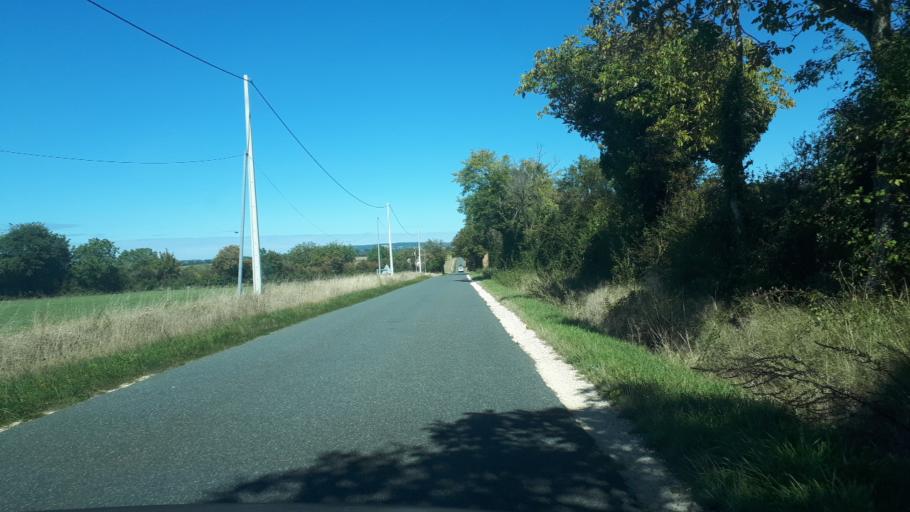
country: FR
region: Centre
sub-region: Departement du Cher
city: Sainte-Solange
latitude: 47.1624
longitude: 2.5677
